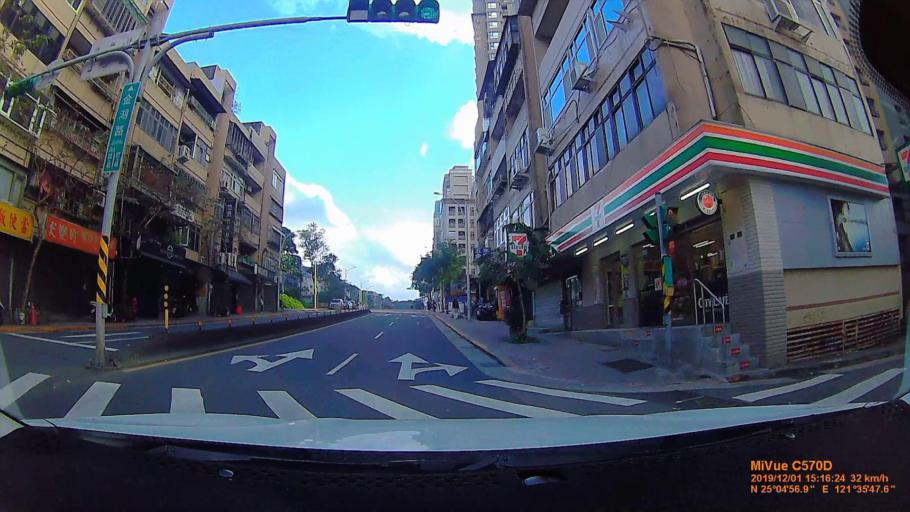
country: TW
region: Taipei
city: Taipei
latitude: 25.0823
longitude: 121.5967
